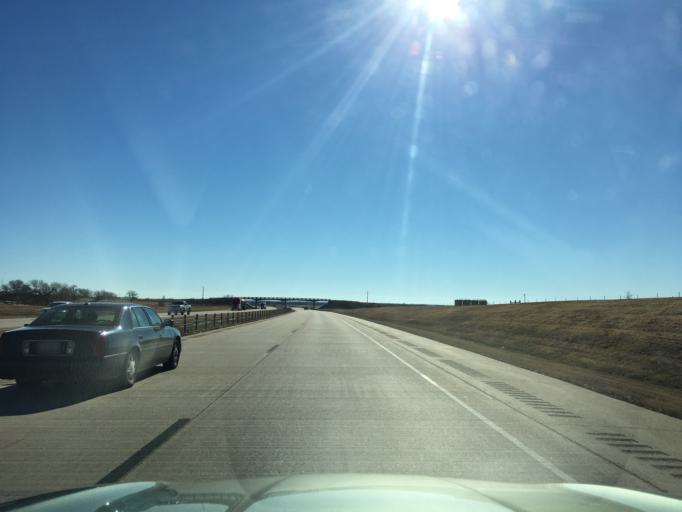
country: US
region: Oklahoma
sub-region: Kay County
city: Tonkawa
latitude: 36.5101
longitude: -97.3371
